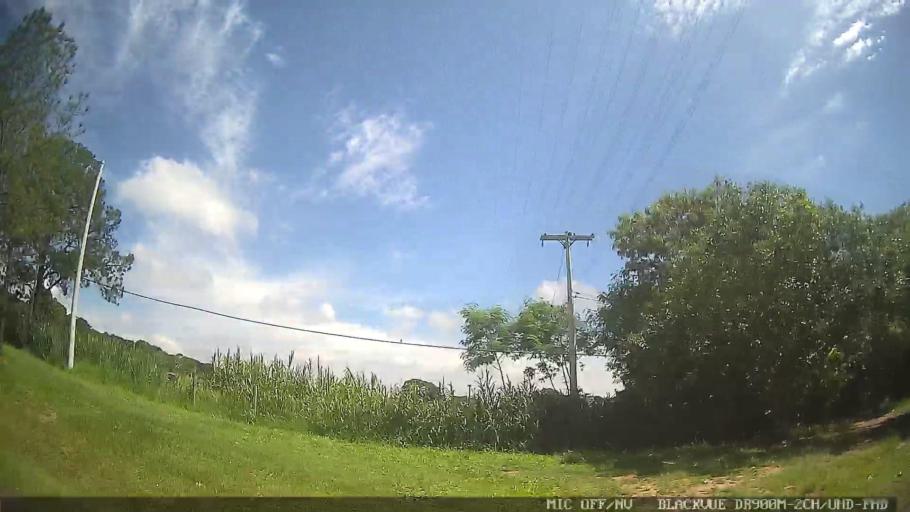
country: BR
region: Sao Paulo
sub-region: Tiete
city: Tiete
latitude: -23.1331
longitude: -47.6892
